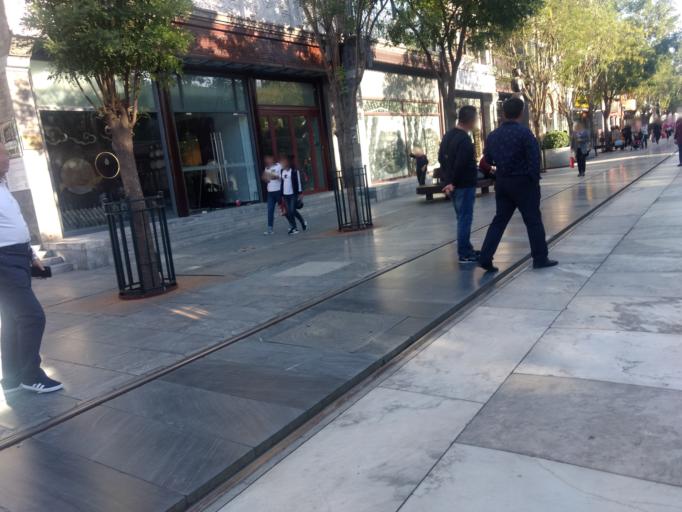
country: CN
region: Beijing
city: Beijing
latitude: 39.8965
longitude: 116.3918
